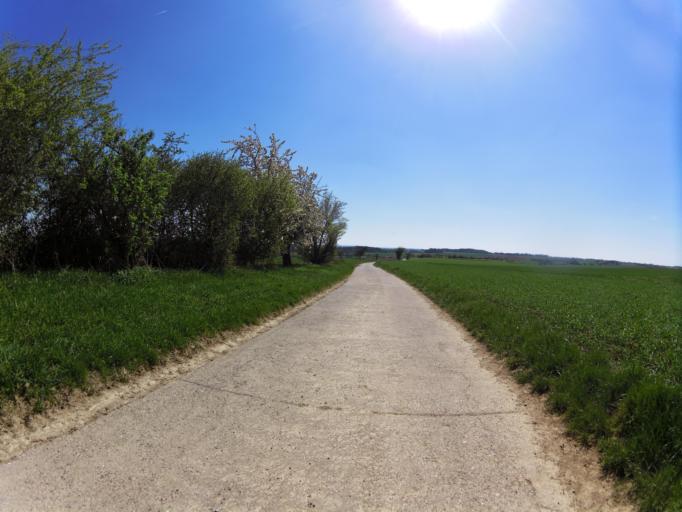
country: DE
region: Bavaria
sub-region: Regierungsbezirk Unterfranken
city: Winterhausen
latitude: 49.6816
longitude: 9.9977
